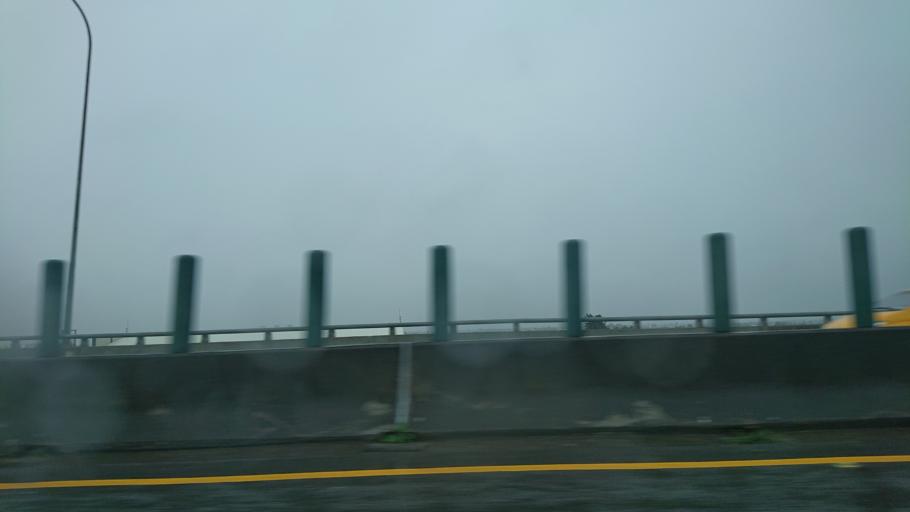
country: TW
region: Taiwan
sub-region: Yunlin
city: Douliu
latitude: 23.7924
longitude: 120.2773
